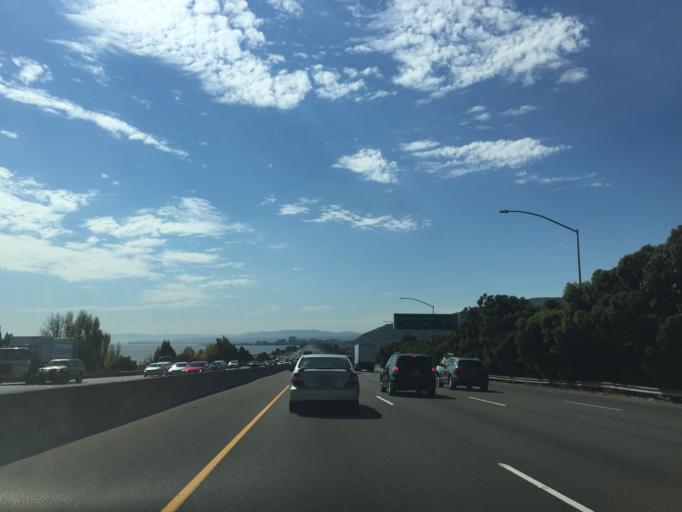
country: US
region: California
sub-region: San Mateo County
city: Brisbane
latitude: 37.7110
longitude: -122.3956
